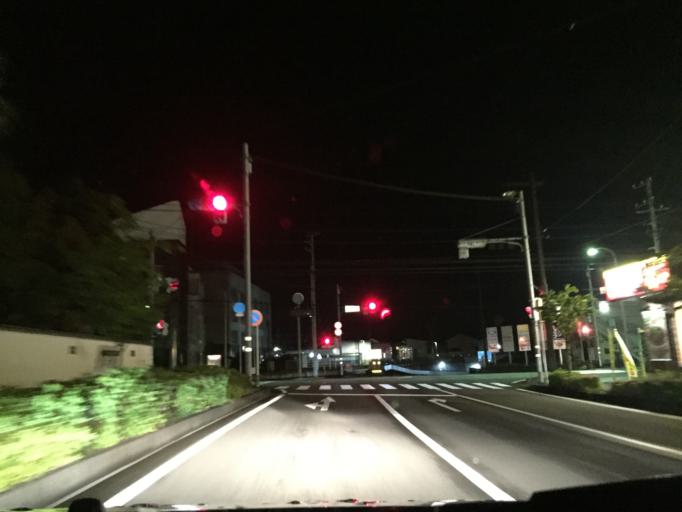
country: JP
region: Shizuoka
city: Mishima
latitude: 35.1666
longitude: 138.9049
